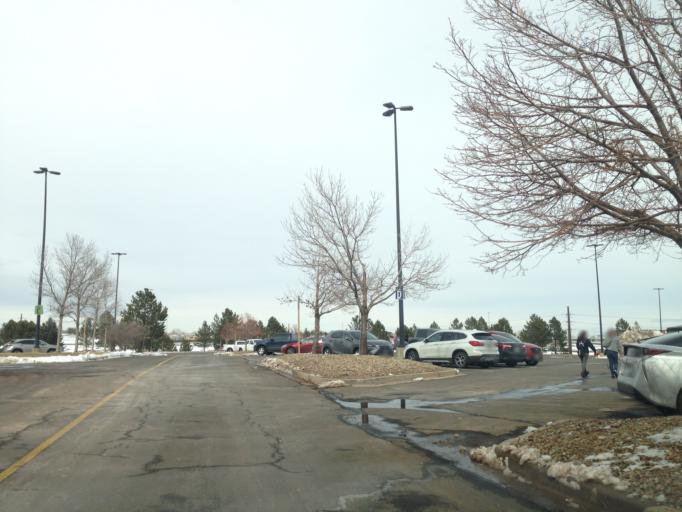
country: US
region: Colorado
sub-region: Boulder County
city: Superior
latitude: 39.9347
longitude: -105.1330
